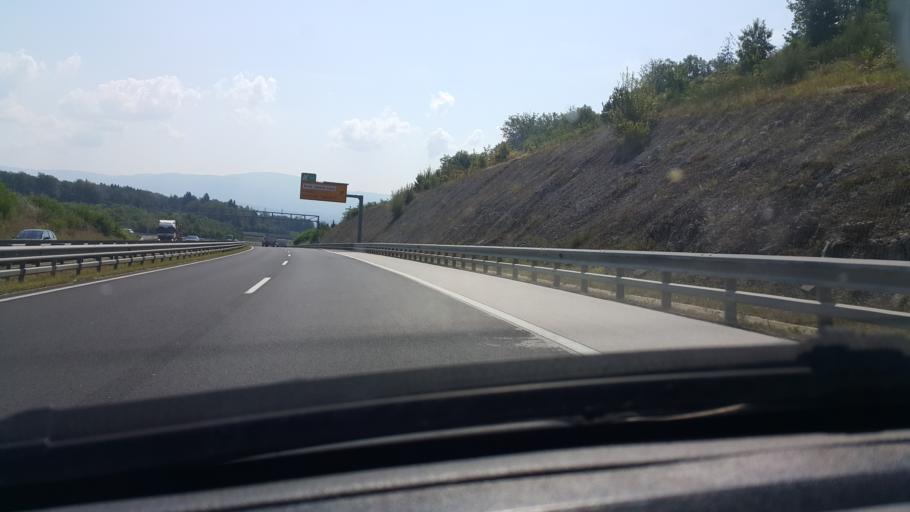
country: SI
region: Novo Mesto
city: Novo Mesto
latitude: 45.8450
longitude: 15.1506
